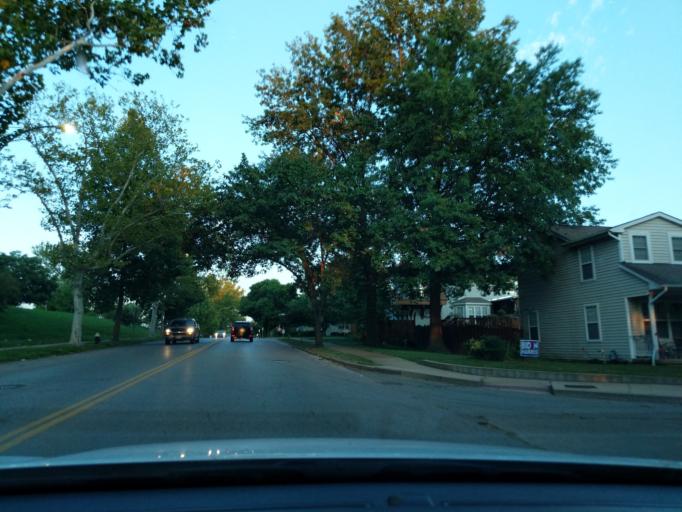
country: US
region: Missouri
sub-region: Saint Louis County
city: Maplewood
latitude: 38.6065
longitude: -90.2840
